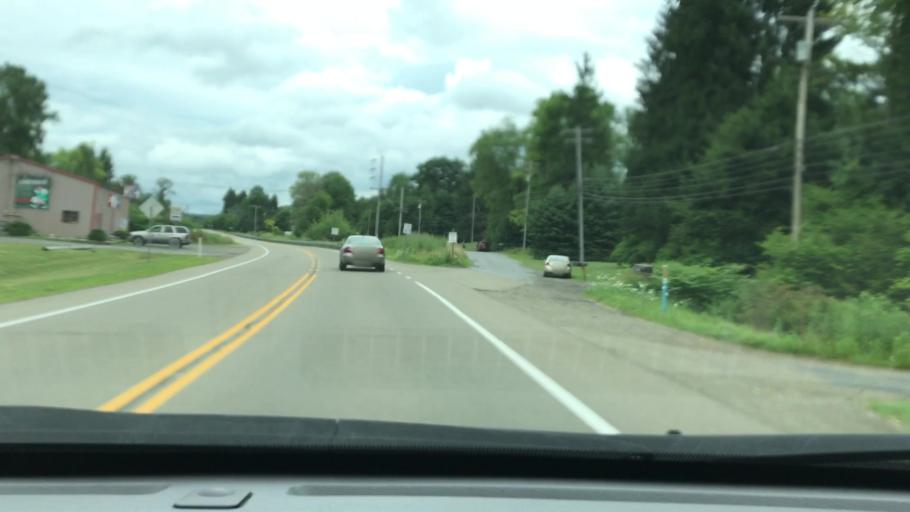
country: US
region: Pennsylvania
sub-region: Elk County
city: Johnsonburg
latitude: 41.5004
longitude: -78.6794
